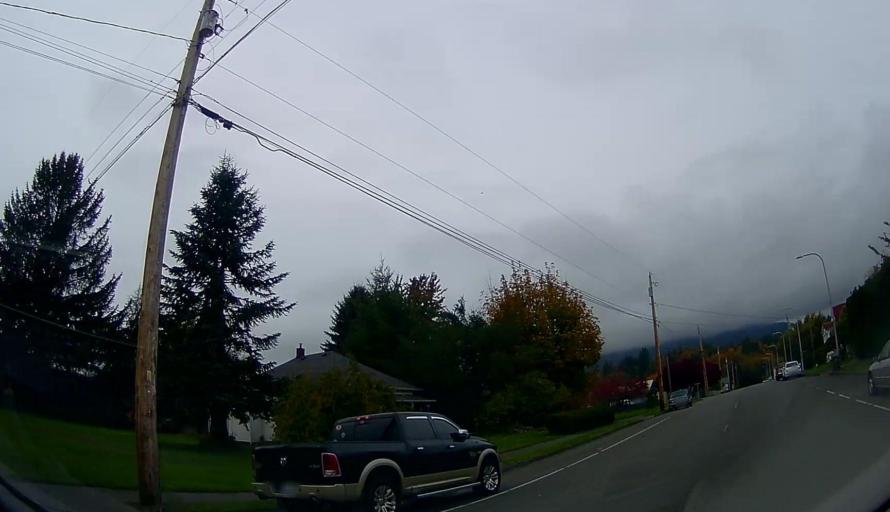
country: US
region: Washington
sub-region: Skagit County
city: Sedro-Woolley
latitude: 48.5239
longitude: -122.0594
